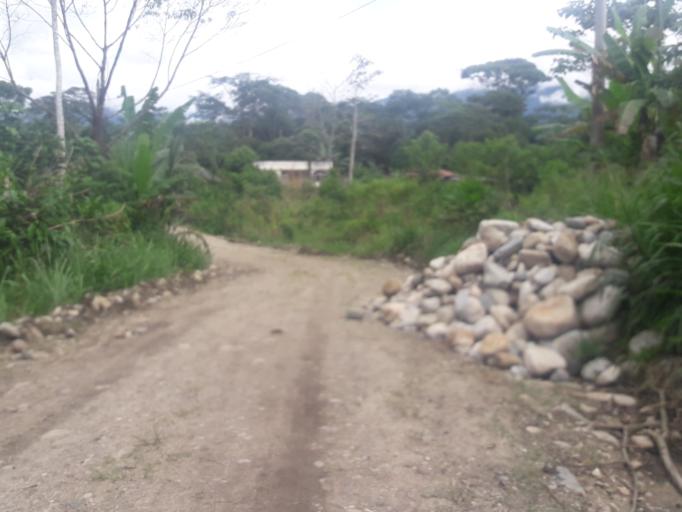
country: EC
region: Napo
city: Tena
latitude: -0.9745
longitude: -77.8443
